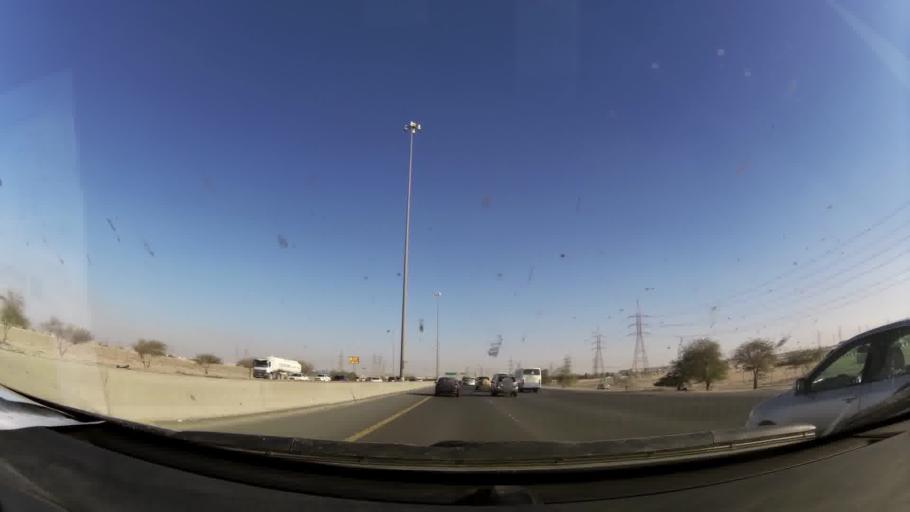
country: KW
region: Al Asimah
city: Ar Rabiyah
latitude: 29.2671
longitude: 47.8302
